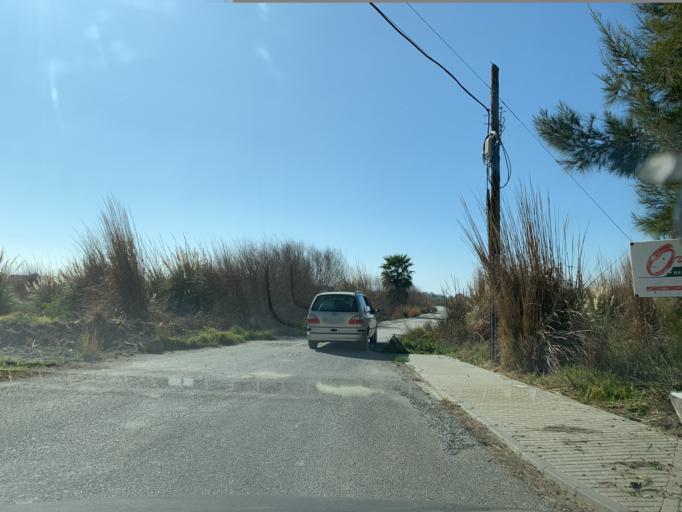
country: ES
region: Andalusia
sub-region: Provincia de Granada
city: El Varadero
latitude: 36.7269
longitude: -3.5470
